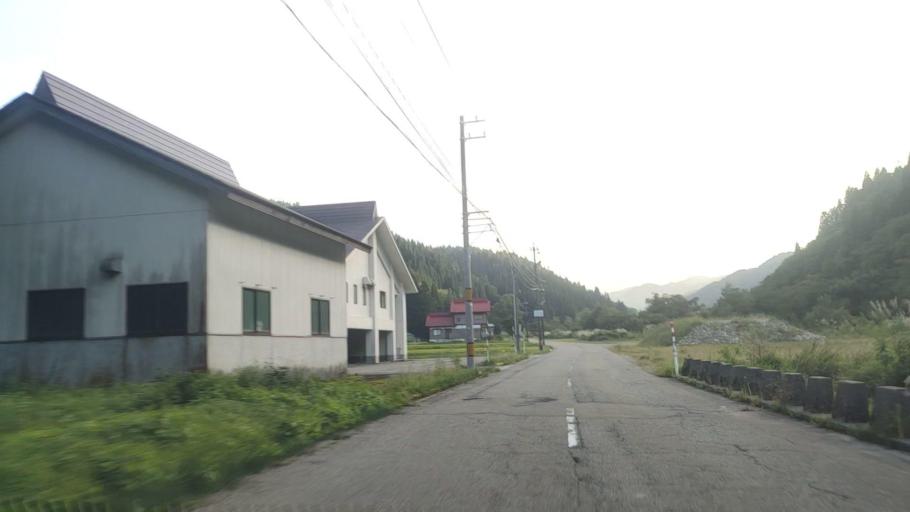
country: JP
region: Toyama
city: Yatsuomachi-higashikumisaka
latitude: 36.4694
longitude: 137.0486
